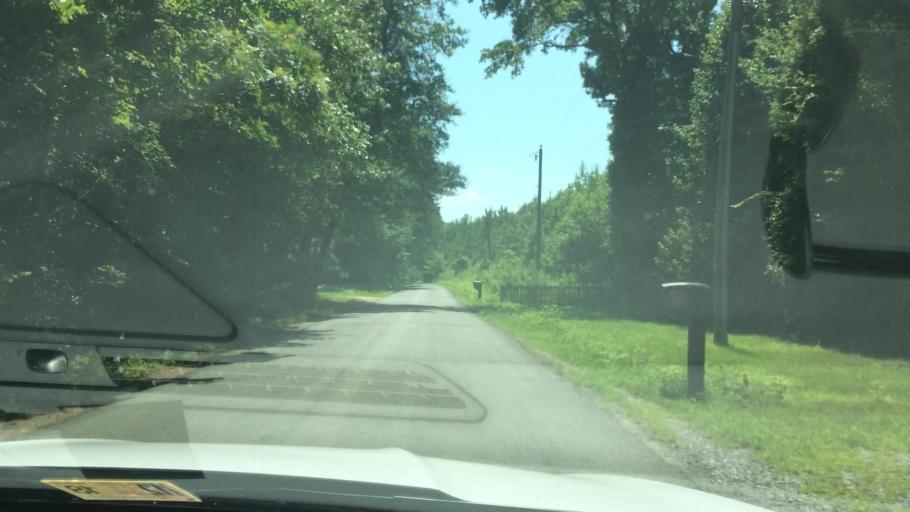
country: US
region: Virginia
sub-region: Charles City County
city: Charles City
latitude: 37.2877
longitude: -76.9649
